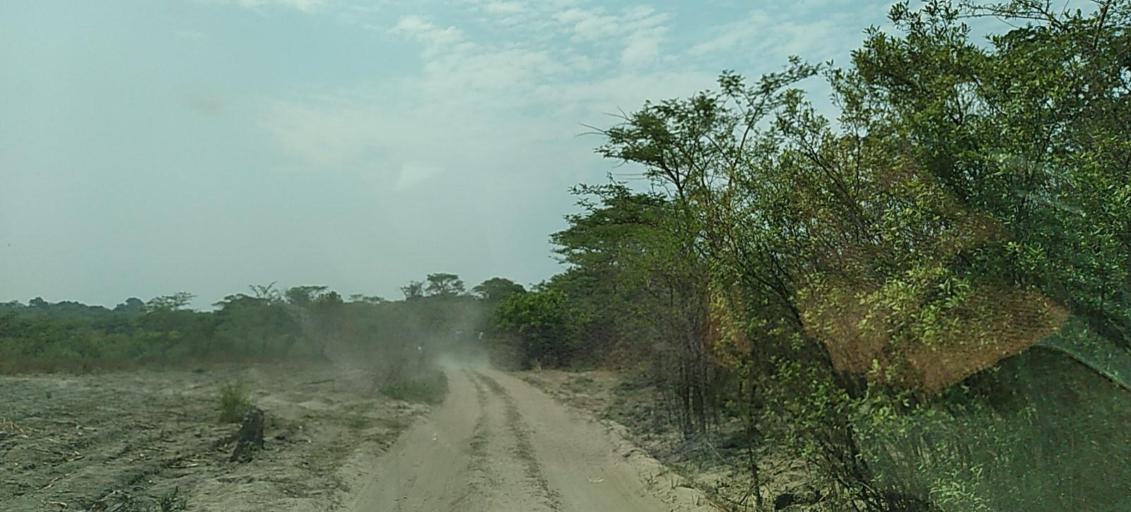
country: ZM
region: Copperbelt
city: Kalulushi
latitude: -12.9285
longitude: 28.1070
